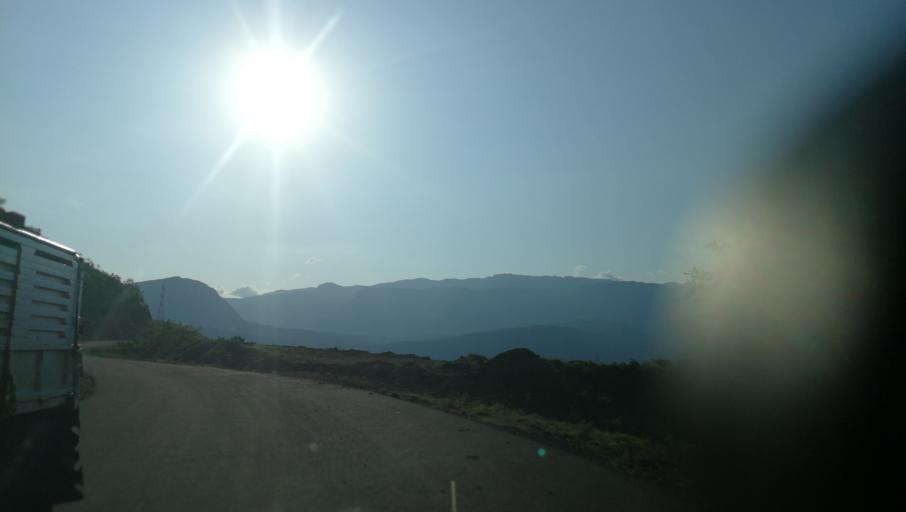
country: ET
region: Southern Nations, Nationalities, and People's Region
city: Areka
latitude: 6.8320
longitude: 37.3145
